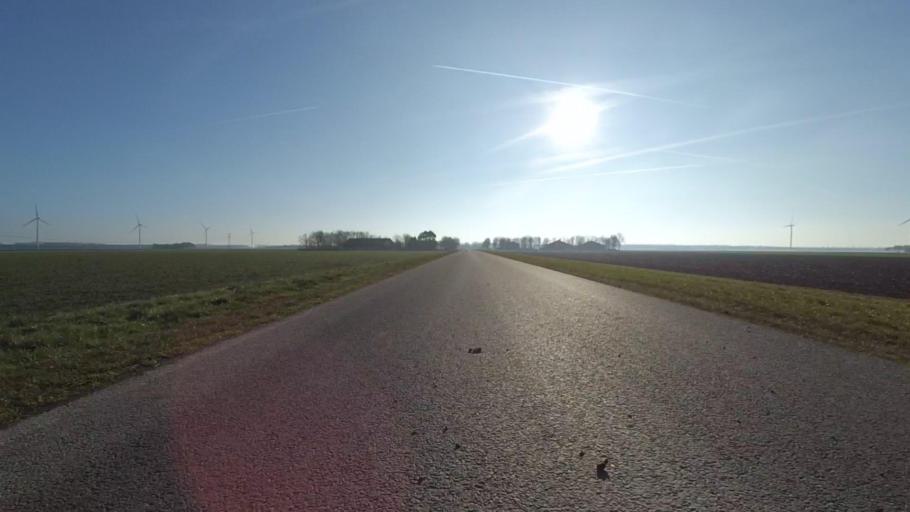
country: NL
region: Utrecht
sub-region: Gemeente Bunschoten
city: Bunschoten
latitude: 52.2971
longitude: 5.4260
